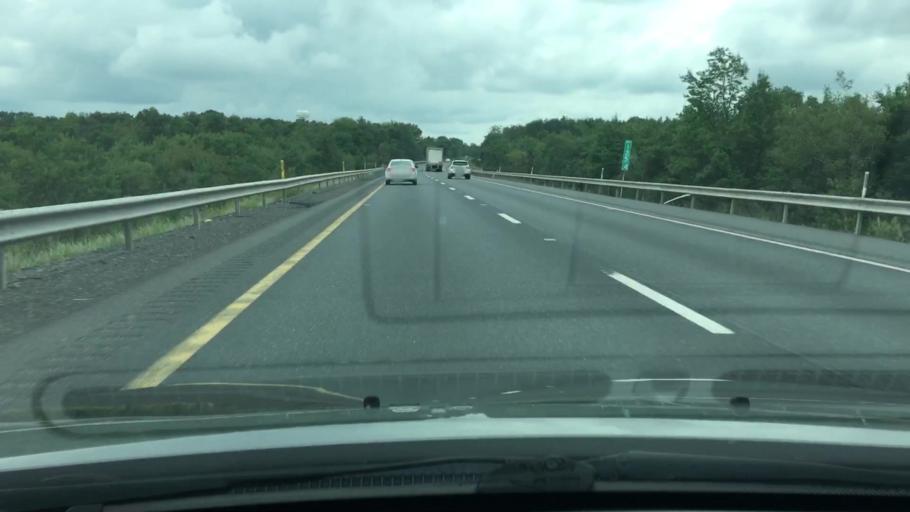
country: US
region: Pennsylvania
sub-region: Schuylkill County
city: Frackville
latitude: 40.7756
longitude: -76.1978
